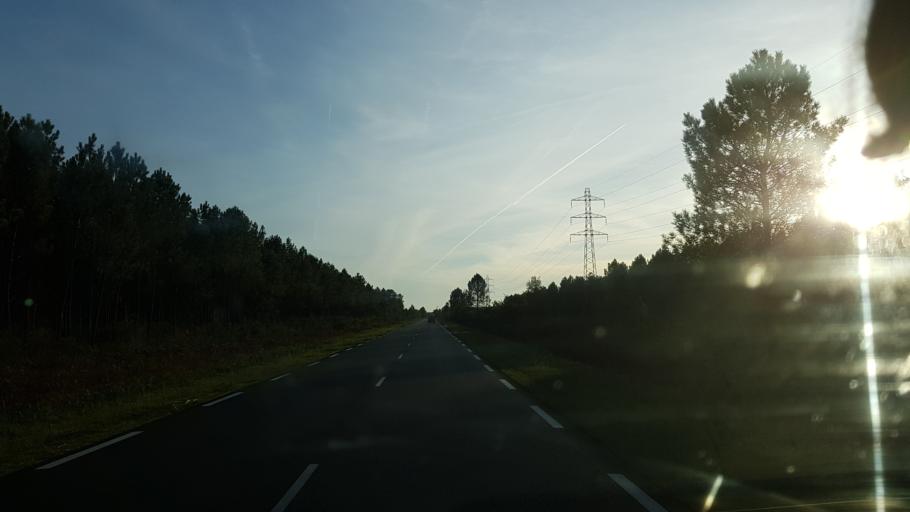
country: FR
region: Aquitaine
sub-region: Departement de la Gironde
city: Martignas-sur-Jalle
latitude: 44.8110
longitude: -0.8591
